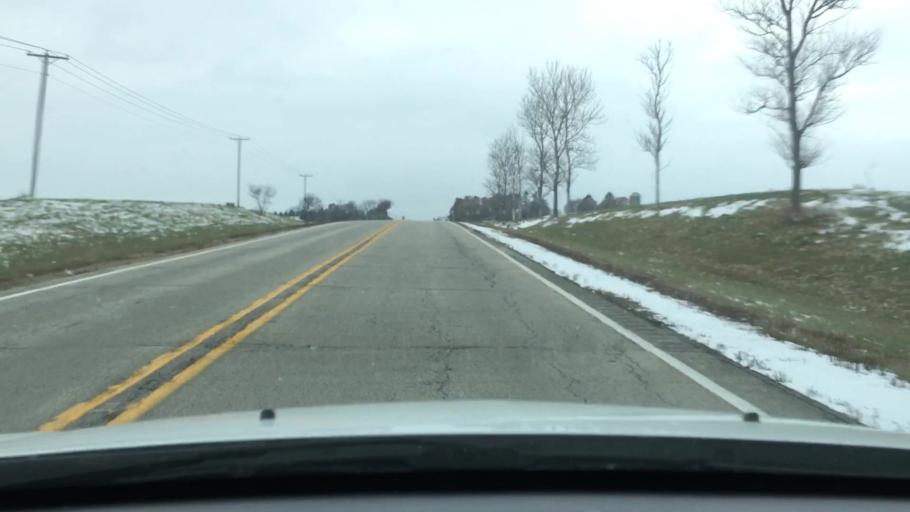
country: US
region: Illinois
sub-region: DeKalb County
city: Malta
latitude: 41.9359
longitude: -88.8390
